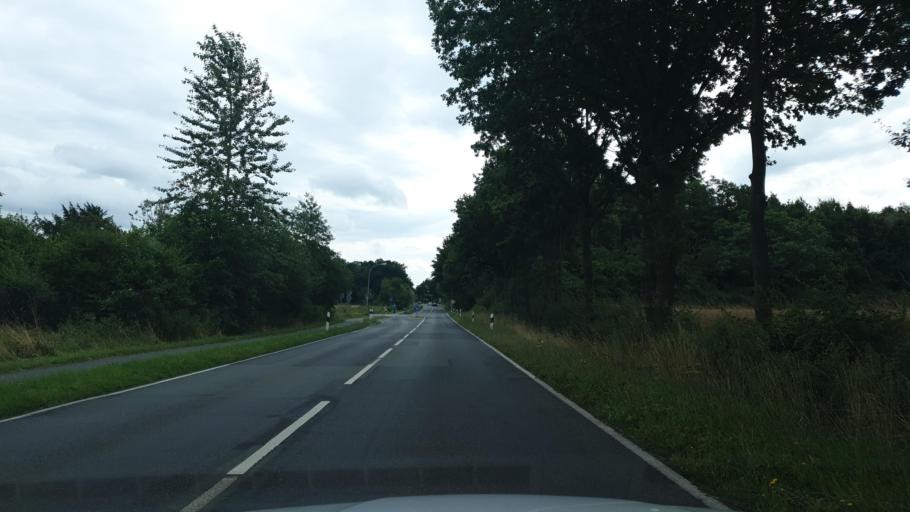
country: DE
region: Lower Saxony
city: Hagen
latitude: 52.2325
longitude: 7.9804
